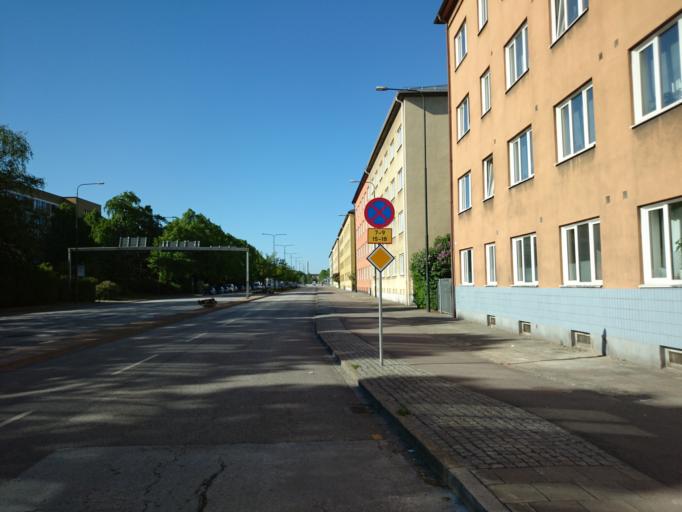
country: SE
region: Skane
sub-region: Malmo
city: Malmoe
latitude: 55.6033
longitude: 13.0277
